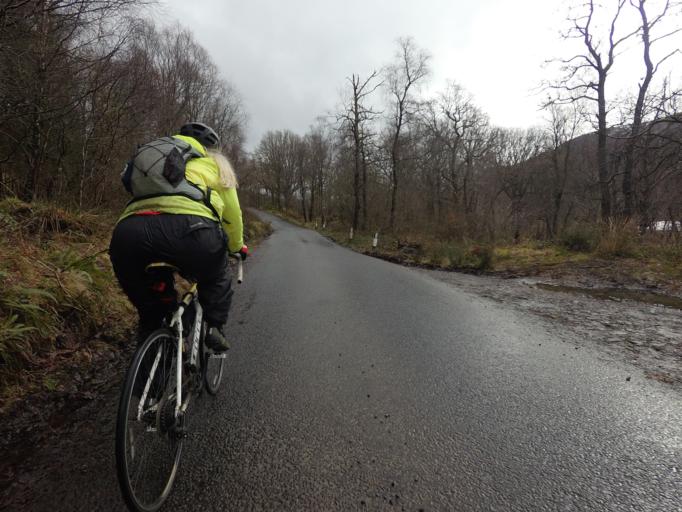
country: GB
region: Scotland
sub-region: West Dunbartonshire
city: Balloch
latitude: 56.2207
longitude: -4.5496
